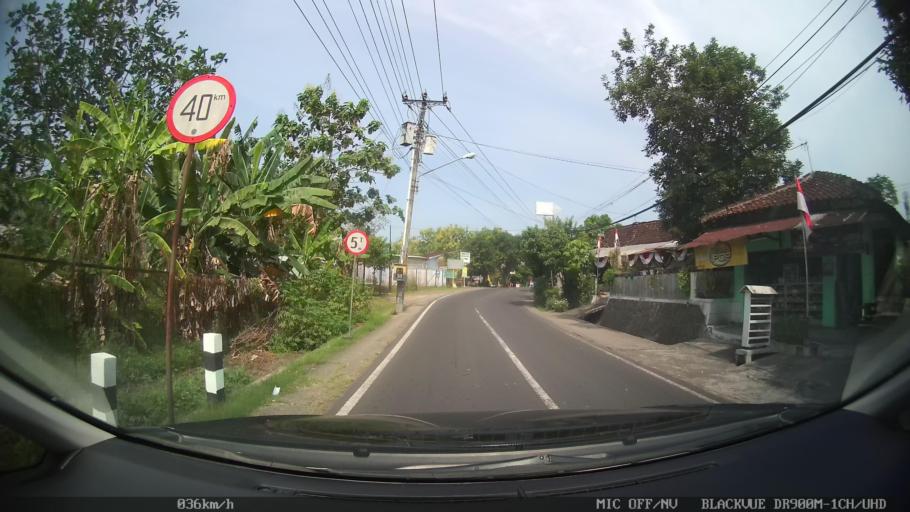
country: ID
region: Daerah Istimewa Yogyakarta
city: Depok
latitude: -7.8036
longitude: 110.4227
